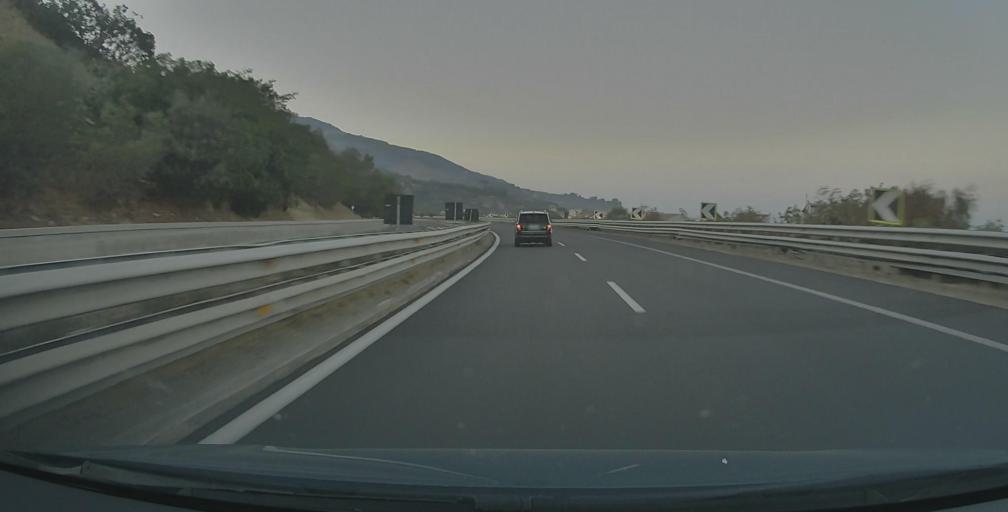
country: IT
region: Sicily
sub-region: Messina
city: Nizza di Sicilia
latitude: 37.9927
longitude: 15.4100
